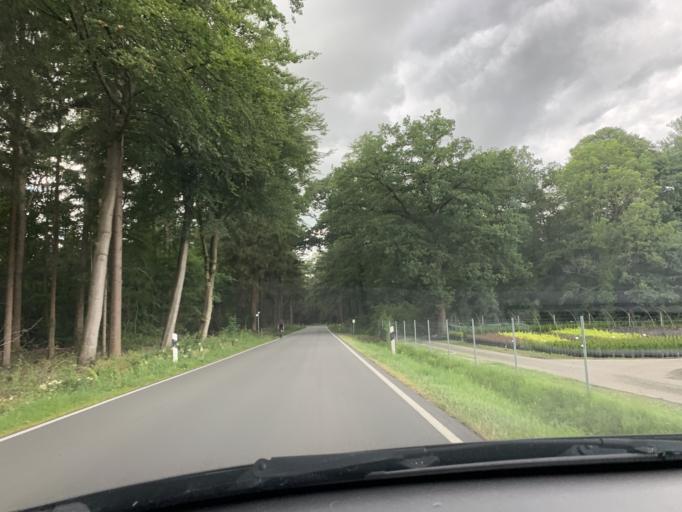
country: DE
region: Lower Saxony
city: Westerstede
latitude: 53.2149
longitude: 7.9228
